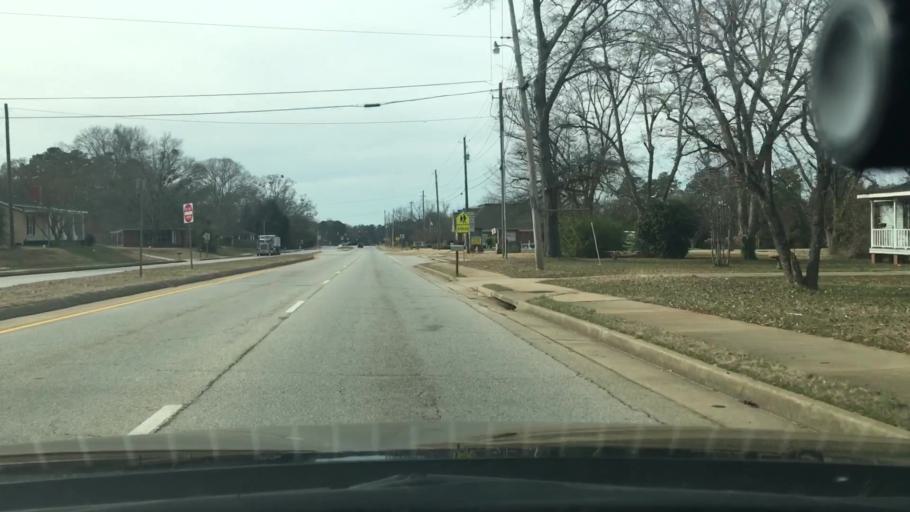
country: US
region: Georgia
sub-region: Spalding County
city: Experiment
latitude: 33.2734
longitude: -84.3017
